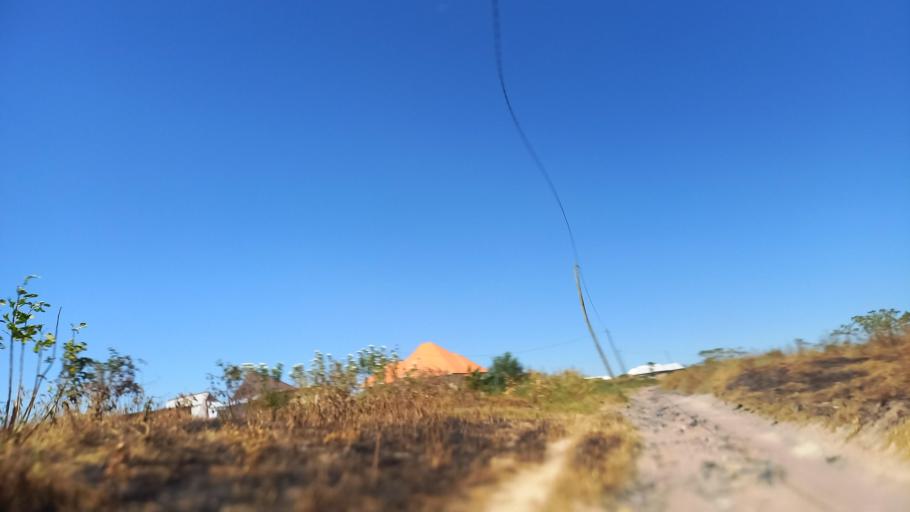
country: TZ
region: Dodoma
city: Dodoma
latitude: -6.1338
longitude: 35.6963
